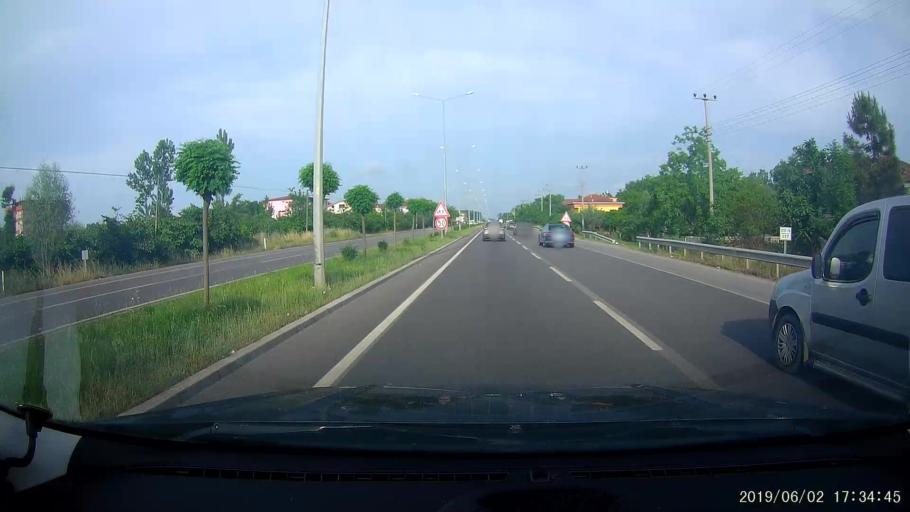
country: TR
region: Samsun
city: Terme
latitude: 41.2200
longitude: 36.8747
